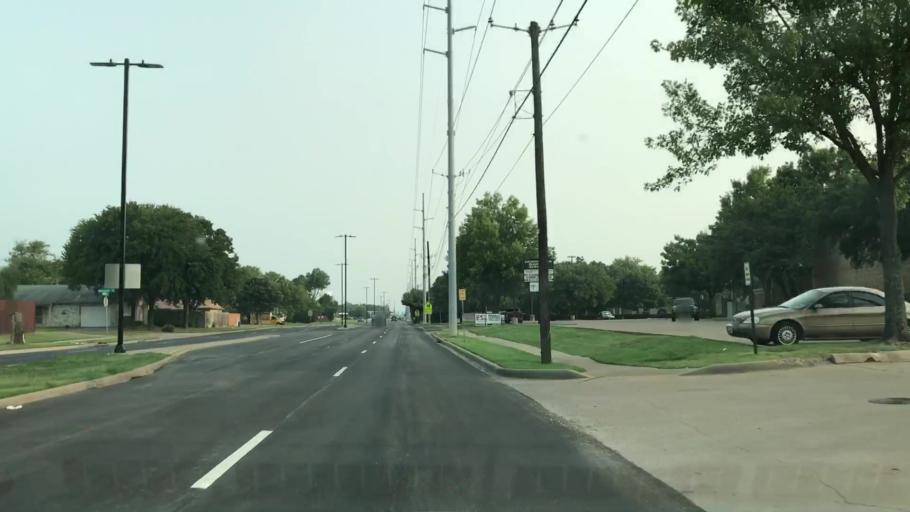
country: US
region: Texas
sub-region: Dallas County
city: Garland
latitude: 32.9276
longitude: -96.6138
